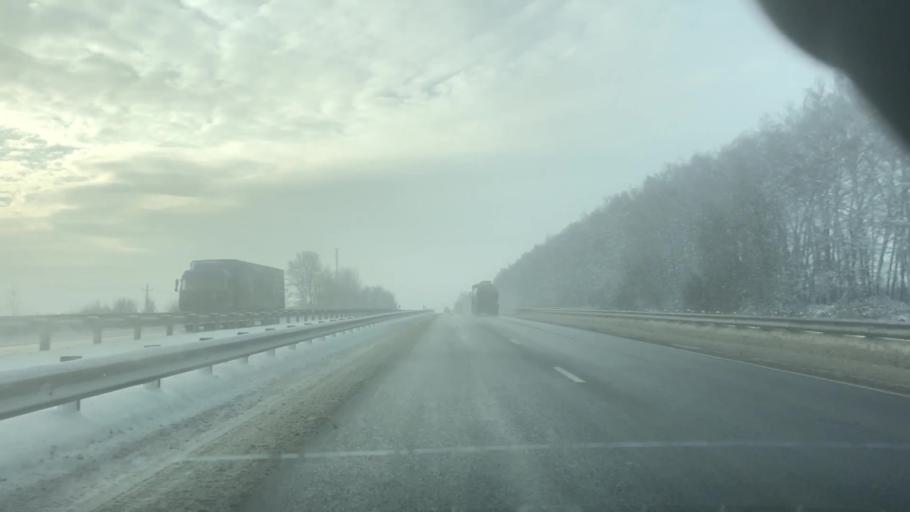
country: RU
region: Tula
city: Venev
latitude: 54.4014
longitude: 38.1631
